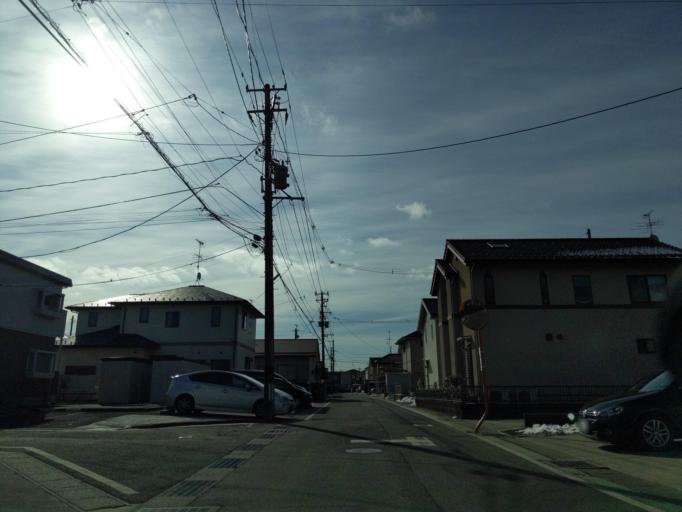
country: JP
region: Fukushima
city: Koriyama
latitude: 37.4175
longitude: 140.3377
